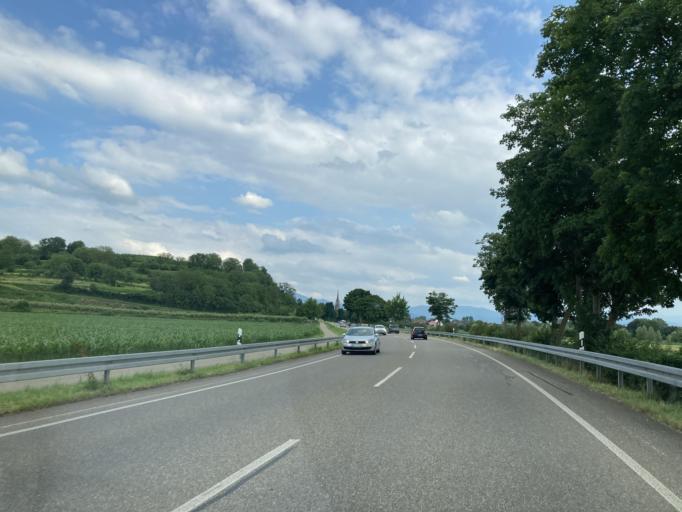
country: DE
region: Baden-Wuerttemberg
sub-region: Freiburg Region
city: Teningen
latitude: 48.1437
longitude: 7.7946
